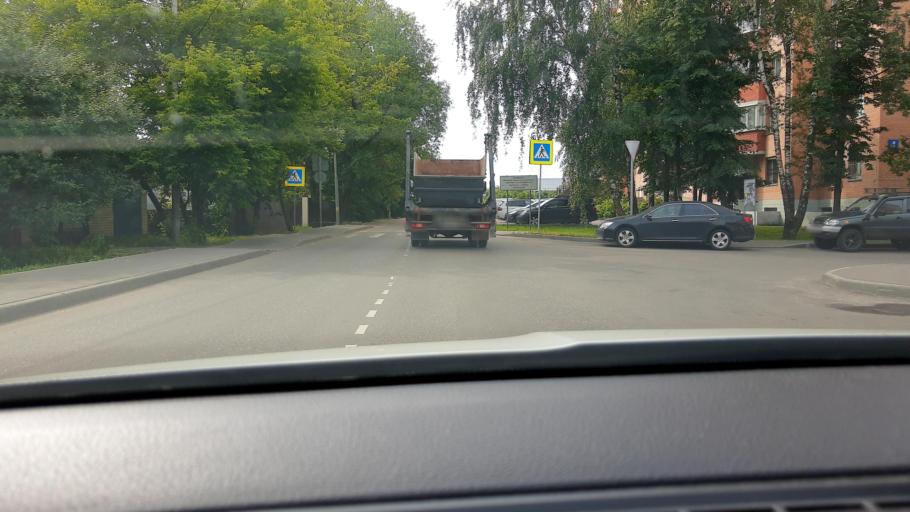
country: RU
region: Moskovskaya
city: Troitsk
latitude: 55.4867
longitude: 37.3076
